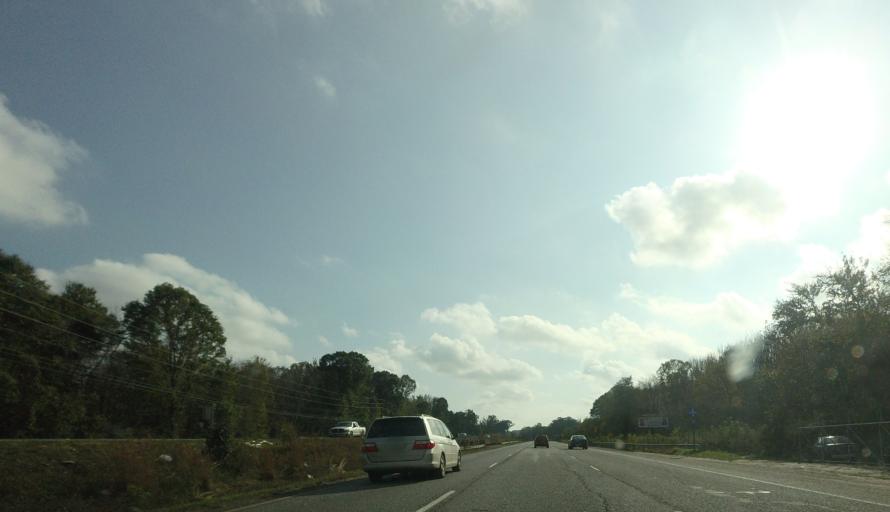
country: US
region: Georgia
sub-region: Bibb County
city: Macon
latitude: 32.7696
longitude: -83.6598
